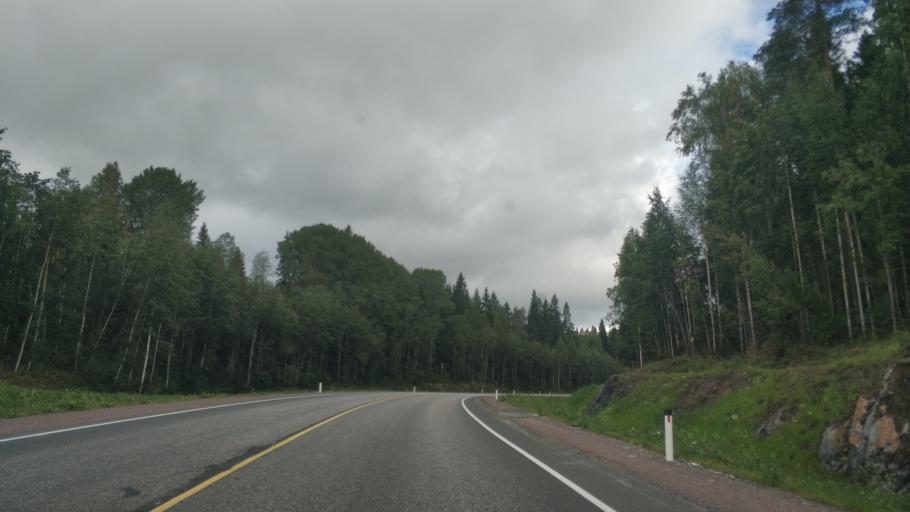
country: RU
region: Republic of Karelia
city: Khelyulya
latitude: 61.8272
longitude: 30.6349
